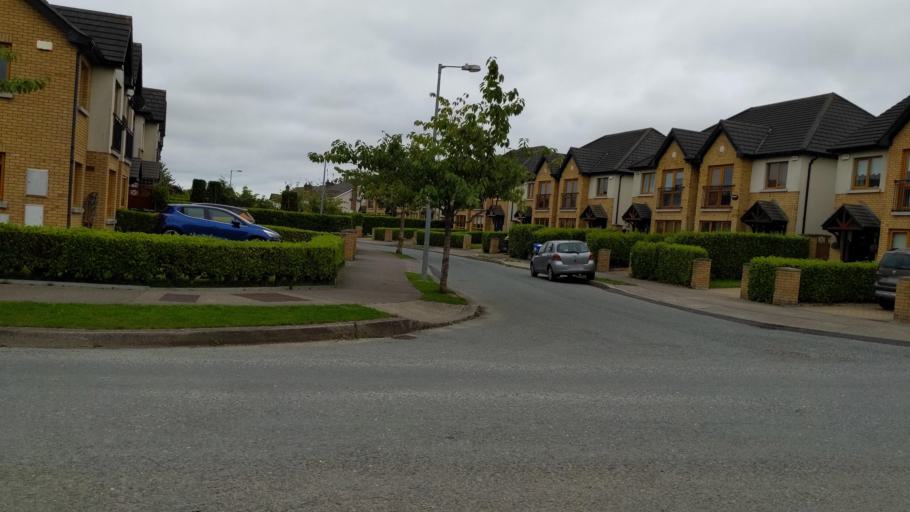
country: IE
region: Leinster
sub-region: Lu
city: Drogheda
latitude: 53.7032
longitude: -6.3539
